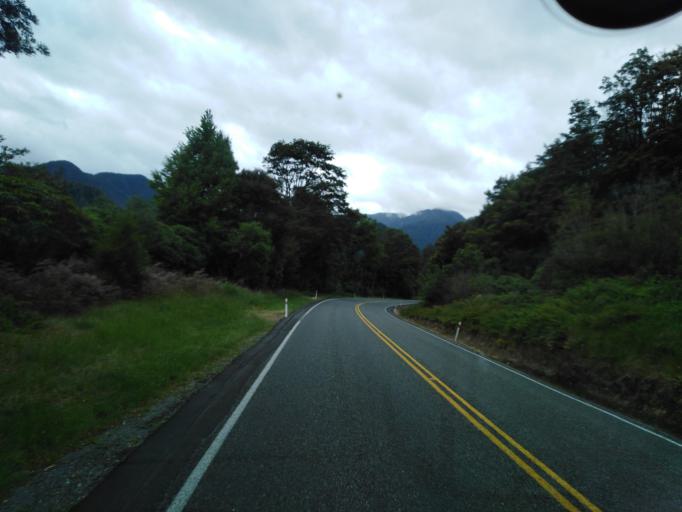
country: NZ
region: Tasman
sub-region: Tasman District
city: Wakefield
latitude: -41.7068
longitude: 172.5845
